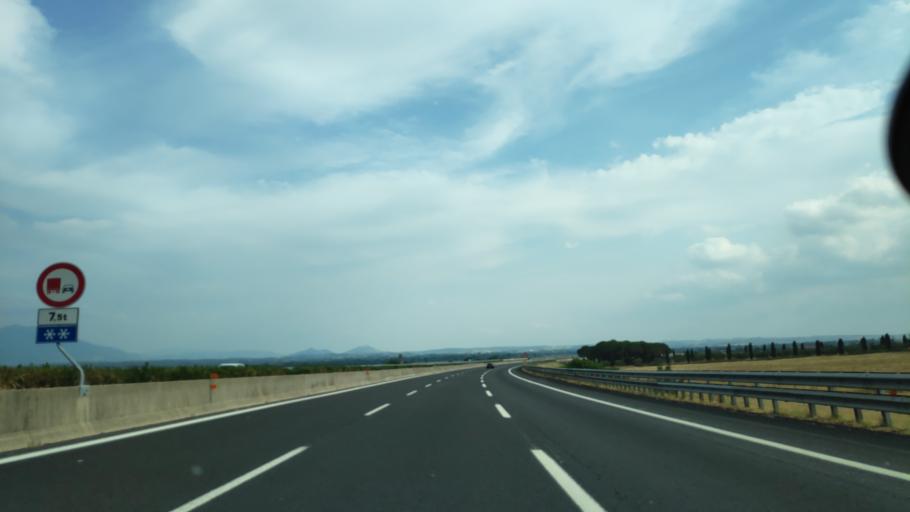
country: IT
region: Latium
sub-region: Citta metropolitana di Roma Capitale
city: Fiano Romano
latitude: 42.1569
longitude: 12.6234
